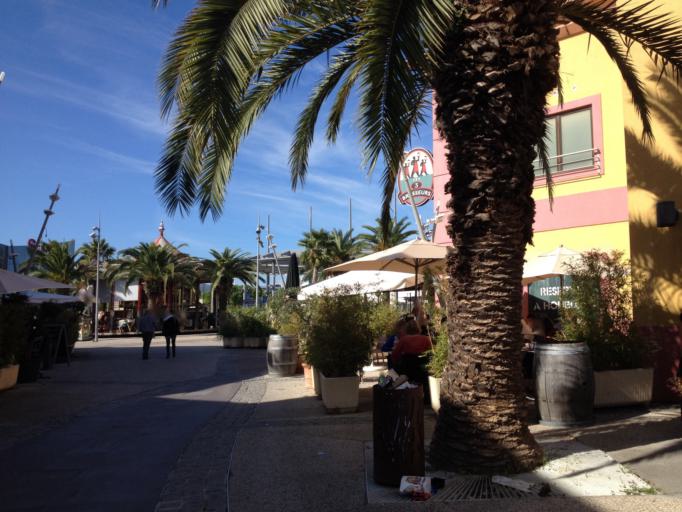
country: FR
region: Languedoc-Roussillon
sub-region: Departement de l'Herault
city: Castelnau-le-Lez
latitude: 43.6035
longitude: 3.9164
